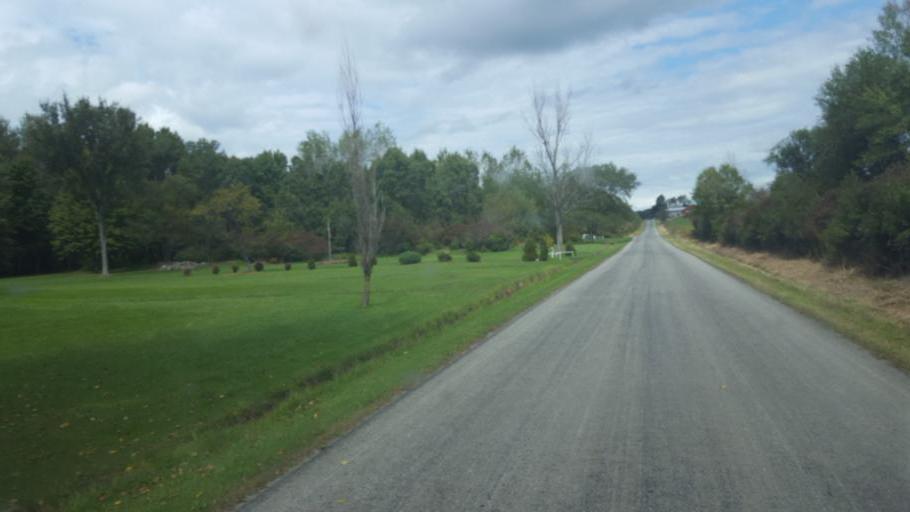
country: US
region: Pennsylvania
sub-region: Crawford County
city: Conneaut Lakeshore
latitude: 41.4904
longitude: -80.2389
